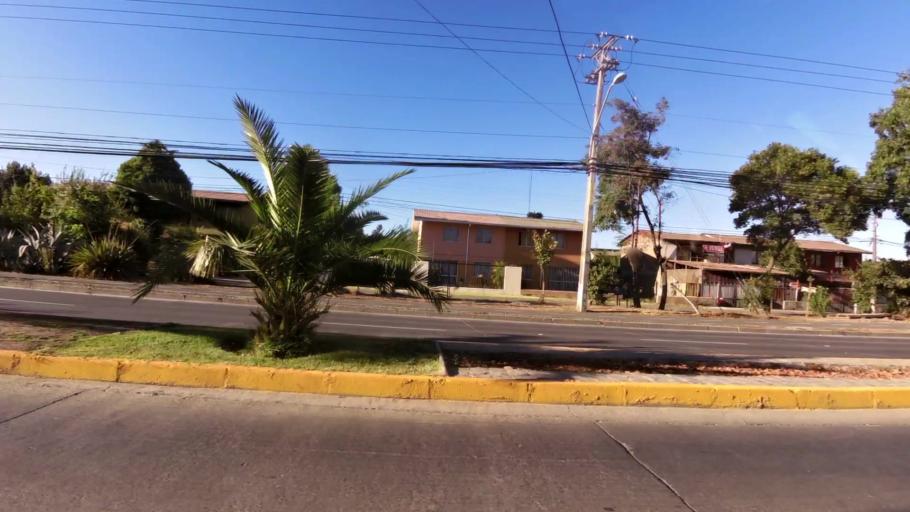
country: CL
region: O'Higgins
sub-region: Provincia de Cachapoal
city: Rancagua
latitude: -34.1743
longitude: -70.7146
